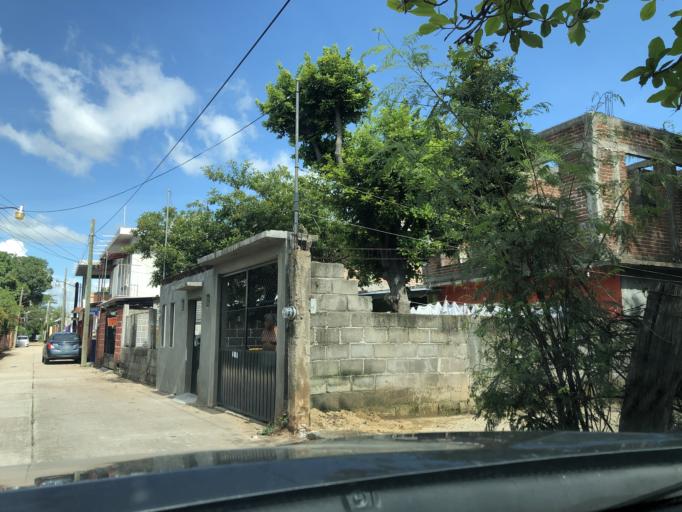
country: MX
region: Oaxaca
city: San Jeronimo Ixtepec
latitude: 16.5582
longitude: -95.1032
